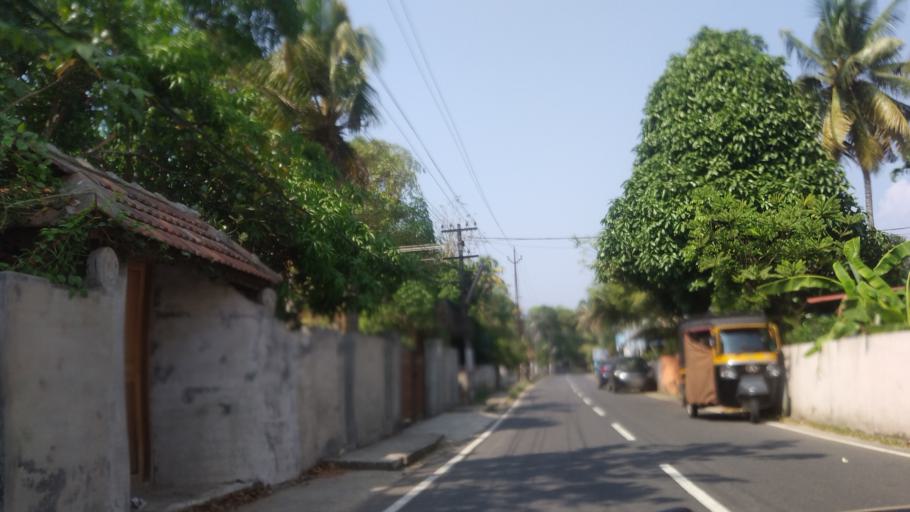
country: IN
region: Kerala
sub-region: Ernakulam
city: Elur
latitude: 10.1316
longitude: 76.2331
